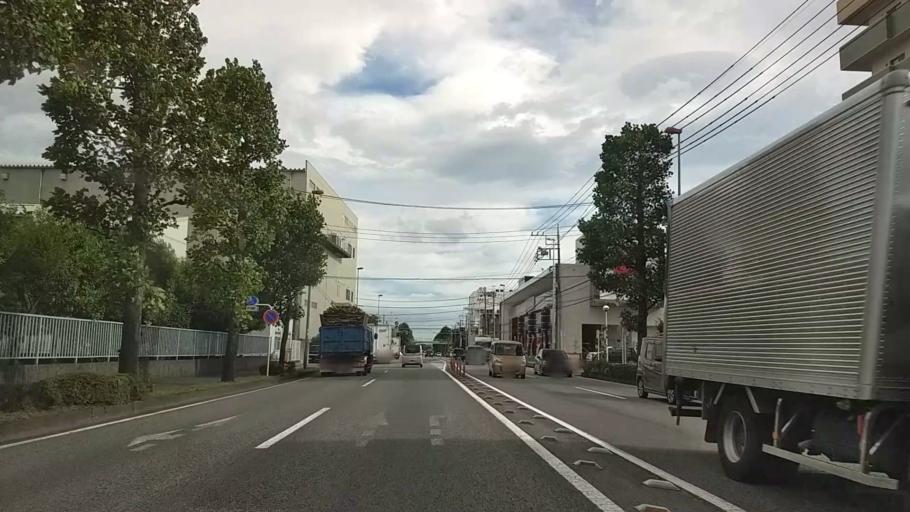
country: JP
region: Tokyo
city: Hachioji
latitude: 35.5818
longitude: 139.3463
